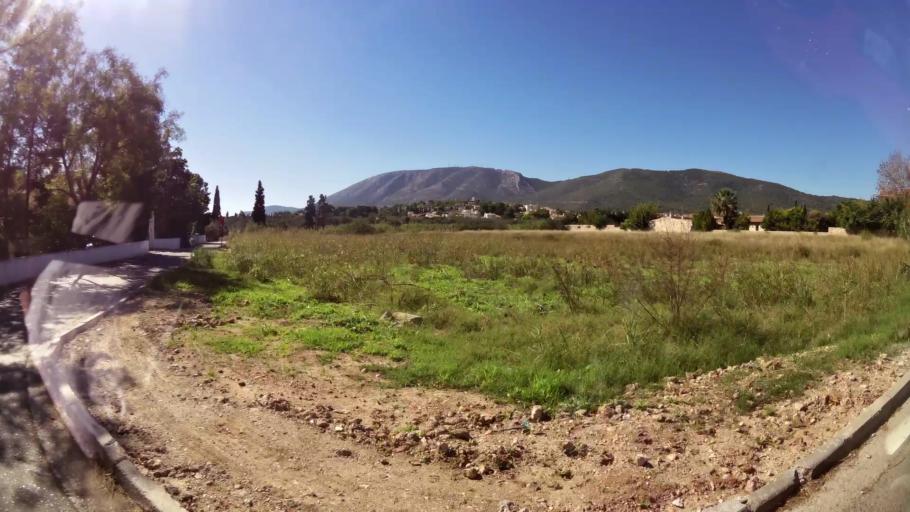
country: GR
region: Attica
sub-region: Nomarchia Anatolikis Attikis
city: Pallini
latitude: 37.9913
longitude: 23.8673
